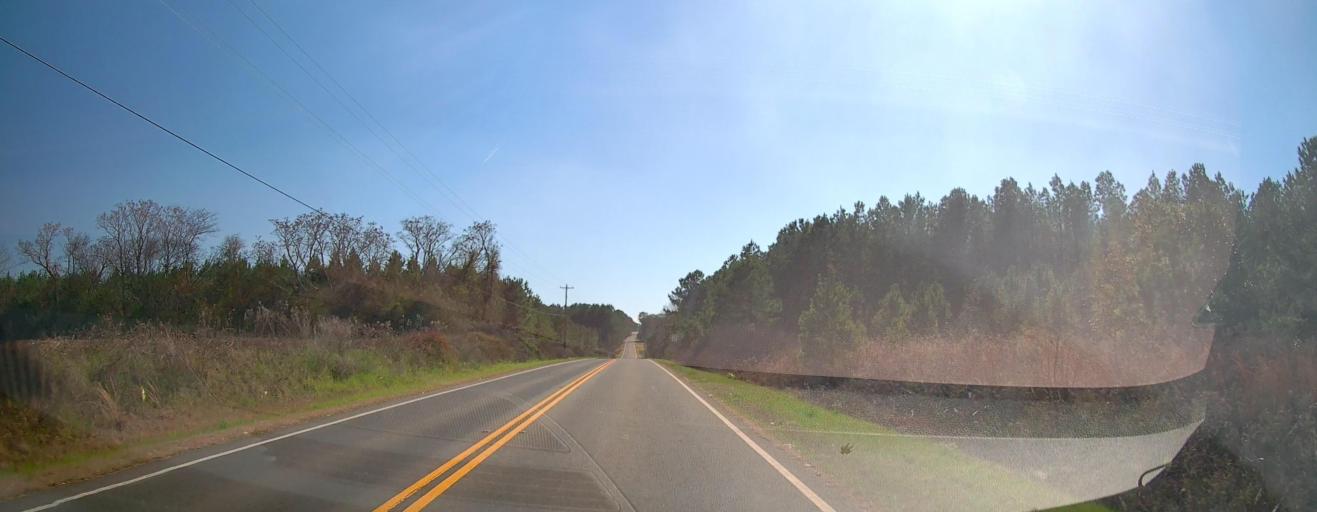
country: US
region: Georgia
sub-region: Macon County
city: Montezuma
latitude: 32.3264
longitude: -84.0223
